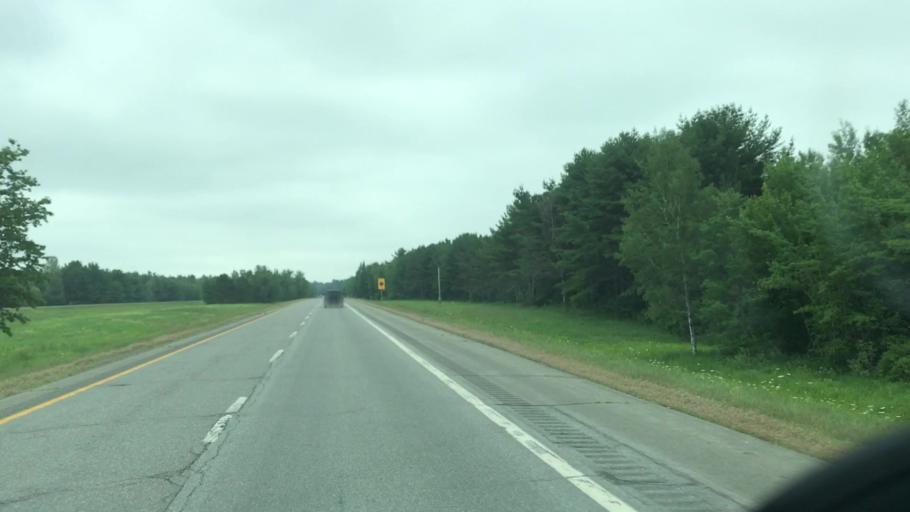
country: US
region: Maine
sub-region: Penobscot County
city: Old Town
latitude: 44.9441
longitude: -68.7076
